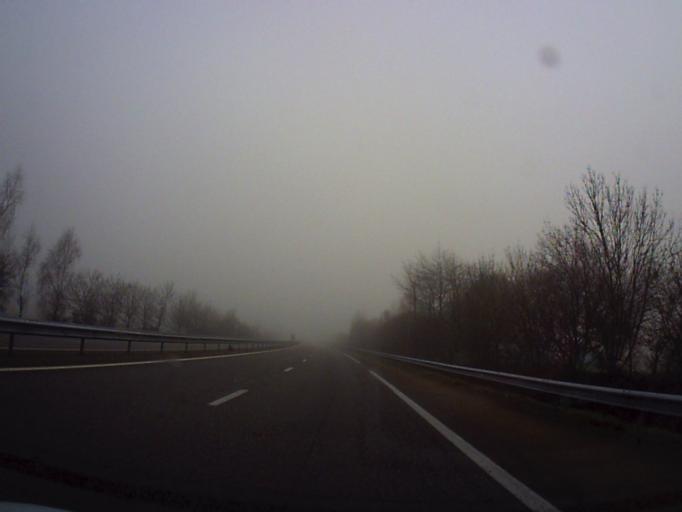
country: FR
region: Brittany
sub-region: Departement du Morbihan
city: Augan
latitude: 47.9403
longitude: -2.2715
